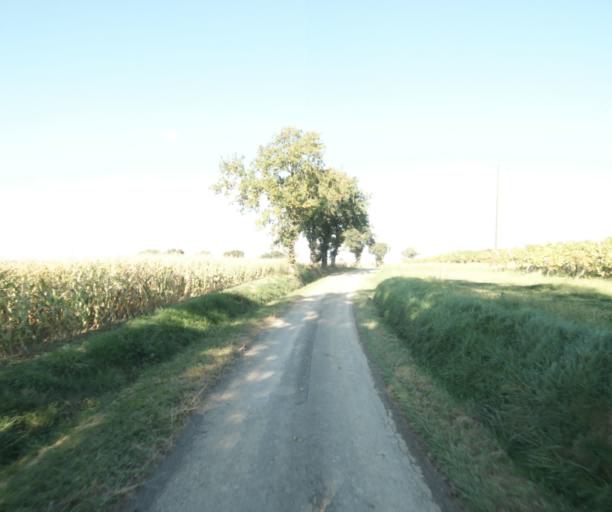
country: FR
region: Midi-Pyrenees
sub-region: Departement du Gers
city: Eauze
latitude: 43.7956
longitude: 0.1243
